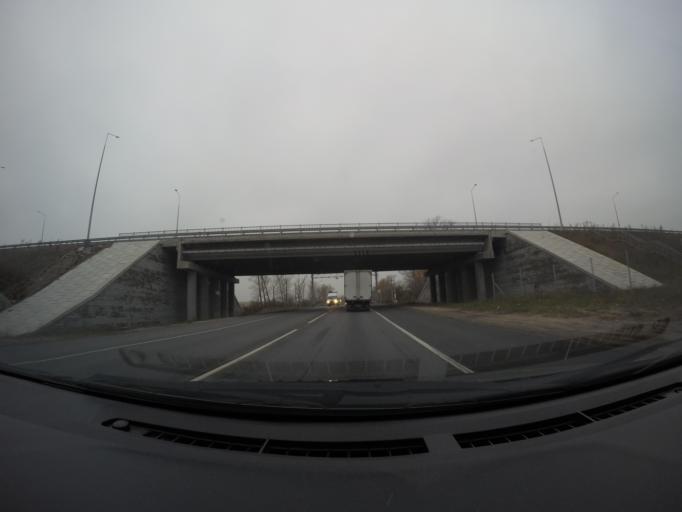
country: RU
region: Moskovskaya
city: Zhitnevo
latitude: 55.3560
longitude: 37.9156
